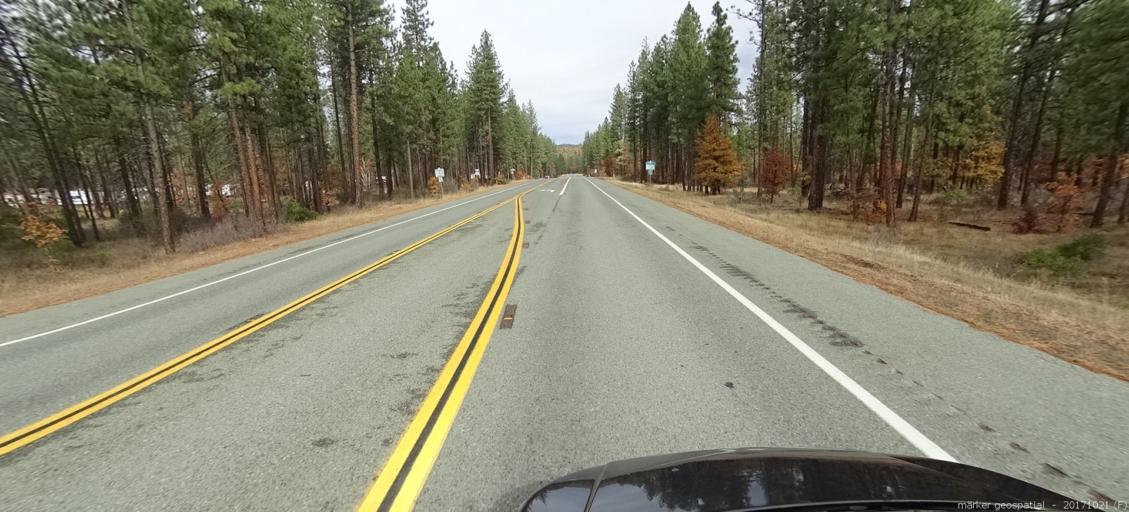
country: US
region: California
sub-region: Shasta County
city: Burney
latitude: 40.9957
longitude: -121.6290
